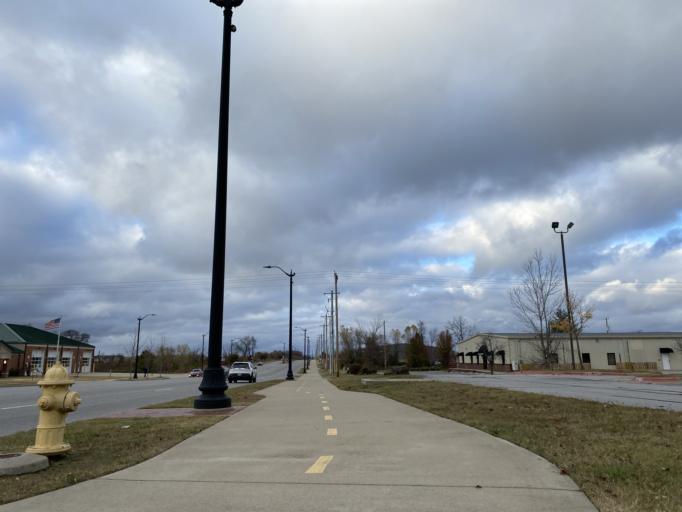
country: US
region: Arkansas
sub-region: Benton County
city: Bentonville
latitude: 36.3371
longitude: -94.2223
